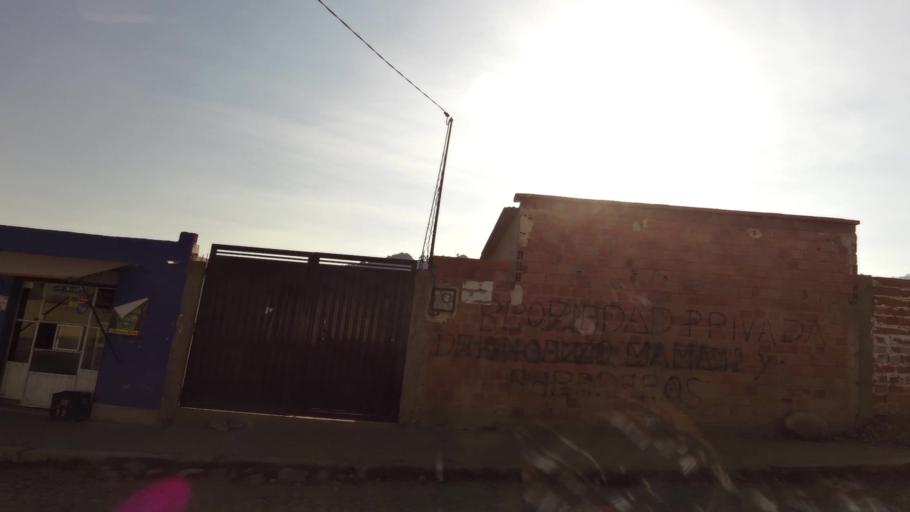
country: BO
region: La Paz
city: La Paz
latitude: -16.5148
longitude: -68.0847
